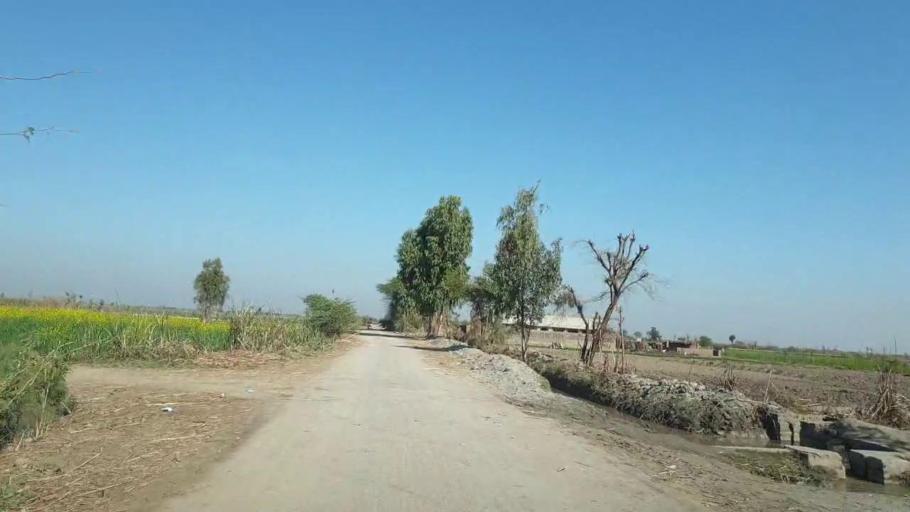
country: PK
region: Sindh
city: Mirpur Khas
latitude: 25.6191
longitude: 69.0239
